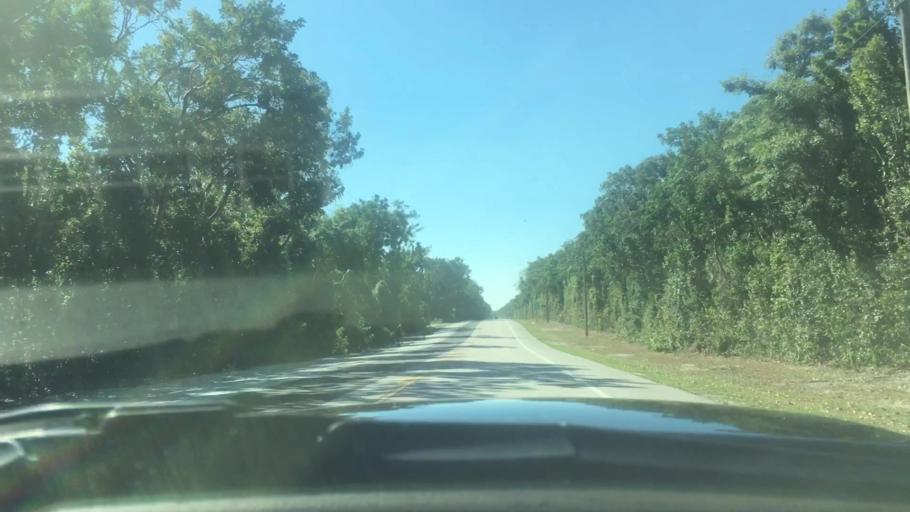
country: US
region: Florida
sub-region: Monroe County
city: North Key Largo
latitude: 25.2403
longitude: -80.3222
